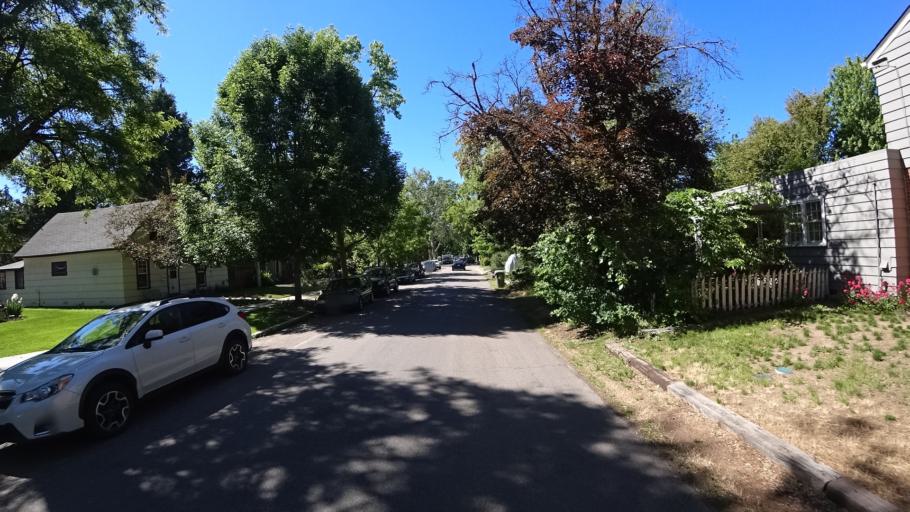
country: US
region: Idaho
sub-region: Ada County
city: Boise
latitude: 43.6372
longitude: -116.2134
